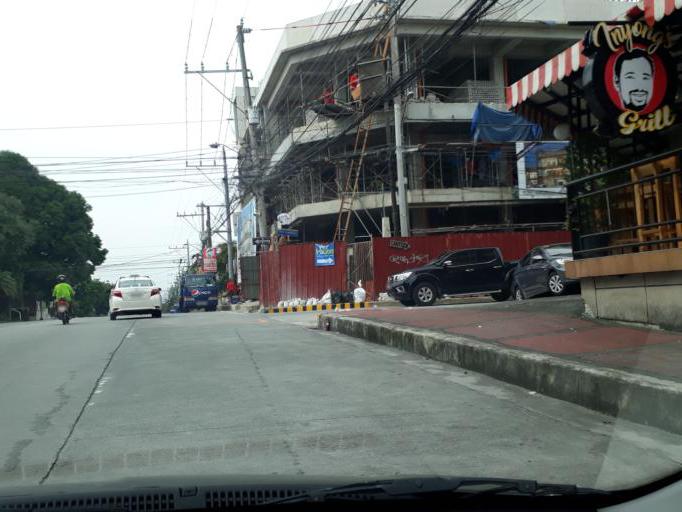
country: PH
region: Calabarzon
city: Del Monte
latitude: 14.6344
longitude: 121.0308
